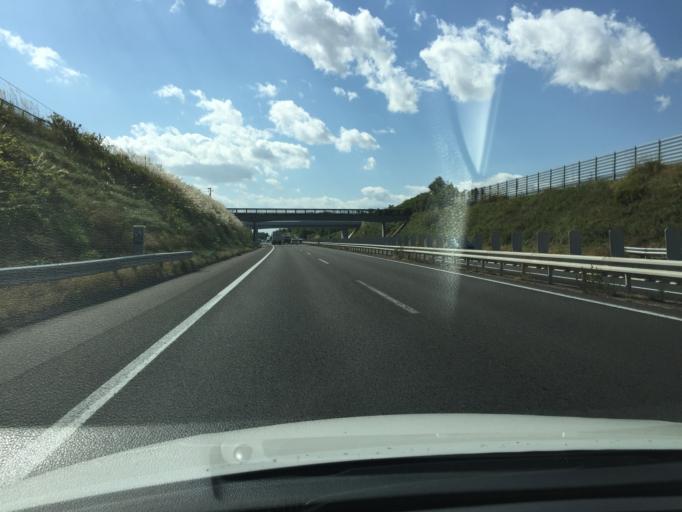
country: JP
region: Fukushima
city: Koriyama
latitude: 37.4588
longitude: 140.3578
